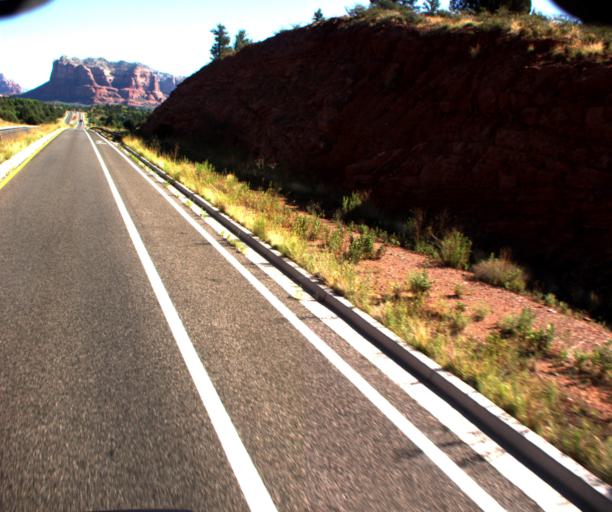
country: US
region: Arizona
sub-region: Yavapai County
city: Big Park
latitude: 34.7626
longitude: -111.7667
